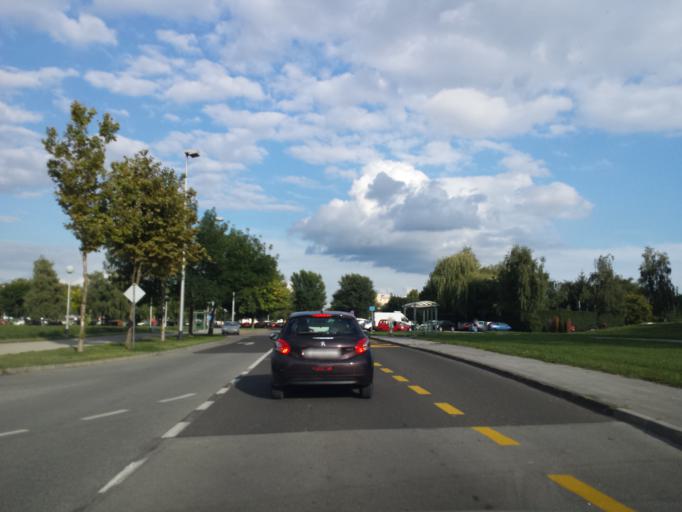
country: HR
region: Grad Zagreb
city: Novi Zagreb
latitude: 45.7901
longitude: 15.9996
